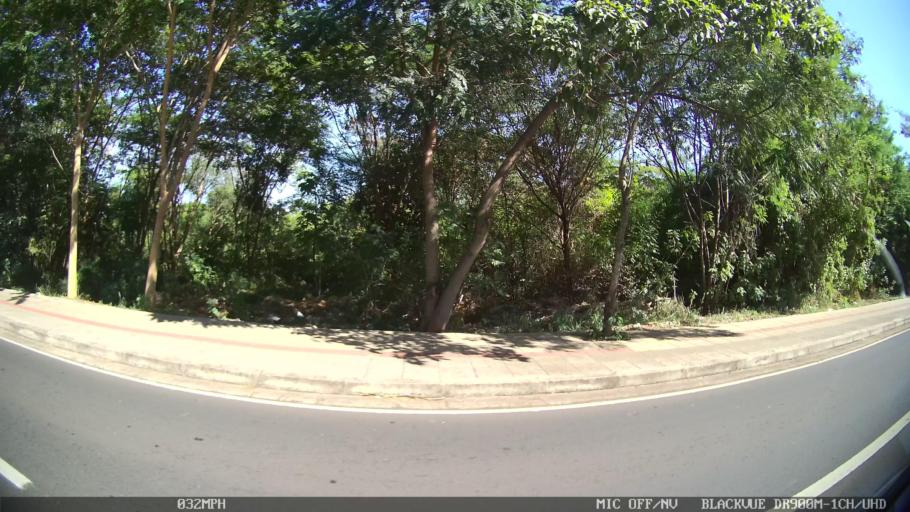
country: BR
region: Sao Paulo
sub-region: Sao Jose Do Rio Preto
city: Sao Jose do Rio Preto
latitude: -20.7810
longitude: -49.3816
